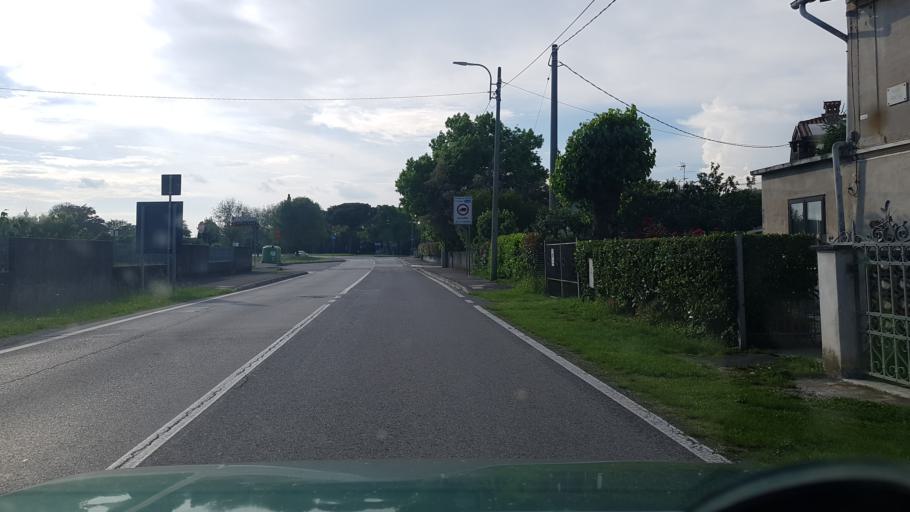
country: IT
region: Friuli Venezia Giulia
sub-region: Provincia di Gorizia
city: Romans d'Isonzo
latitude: 45.8891
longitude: 13.4502
